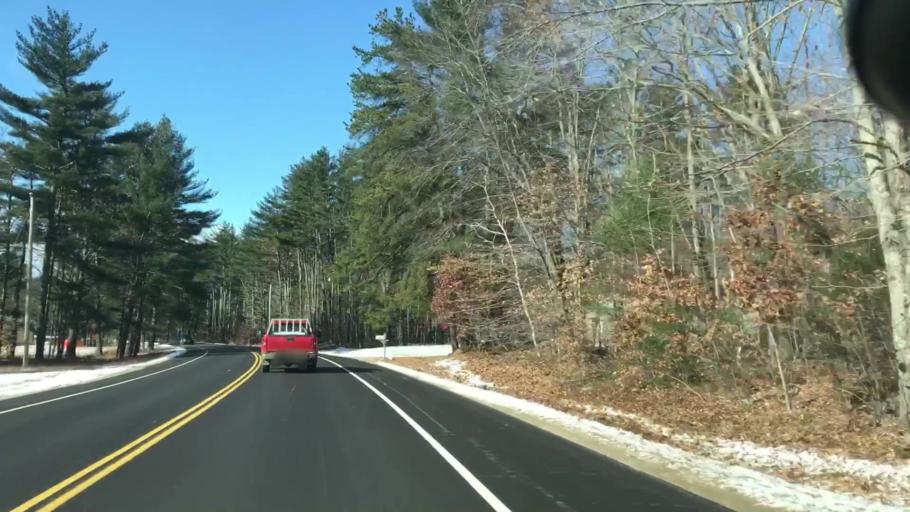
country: US
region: New Hampshire
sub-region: Carroll County
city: Freedom
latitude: 43.7980
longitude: -71.0032
